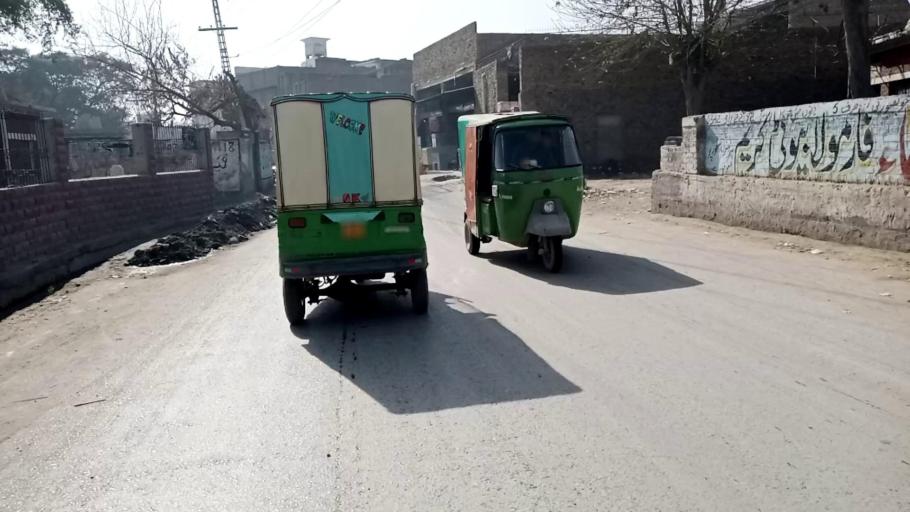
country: PK
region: Khyber Pakhtunkhwa
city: Peshawar
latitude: 34.0032
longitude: 71.5853
